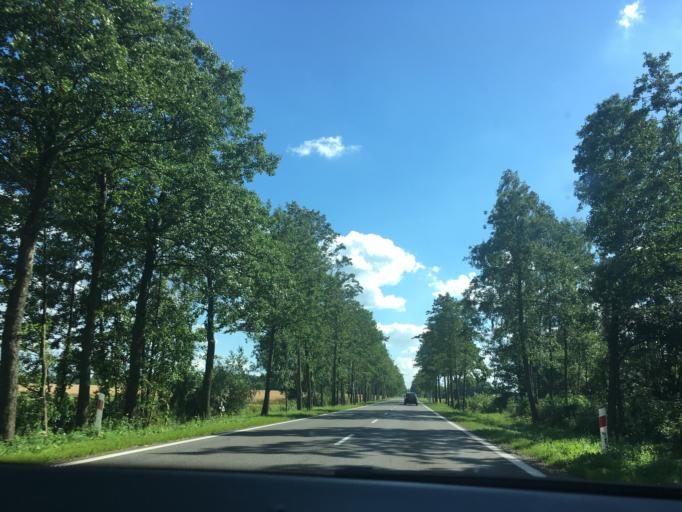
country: PL
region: Podlasie
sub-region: Powiat sokolski
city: Janow
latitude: 53.3848
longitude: 23.1120
